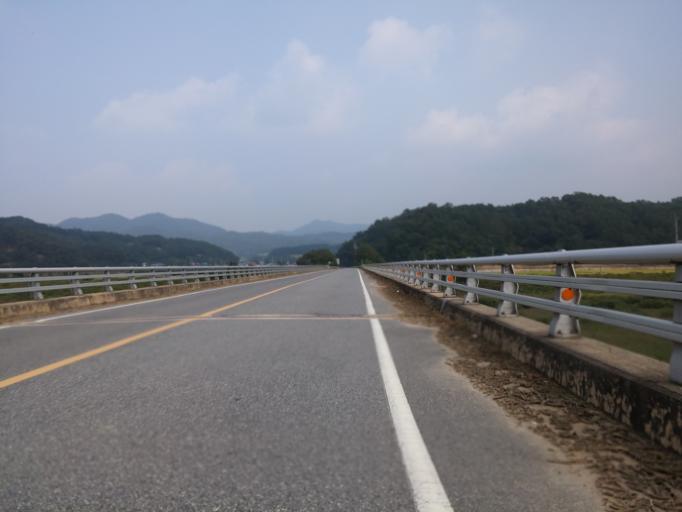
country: KR
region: Chungcheongbuk-do
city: Yong-dong
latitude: 36.3491
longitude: 127.8147
